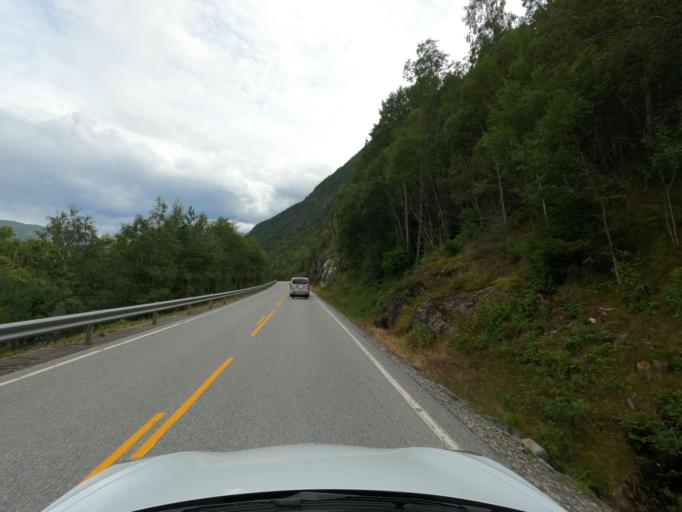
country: NO
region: Telemark
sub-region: Tinn
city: Rjukan
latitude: 59.9256
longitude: 8.8556
